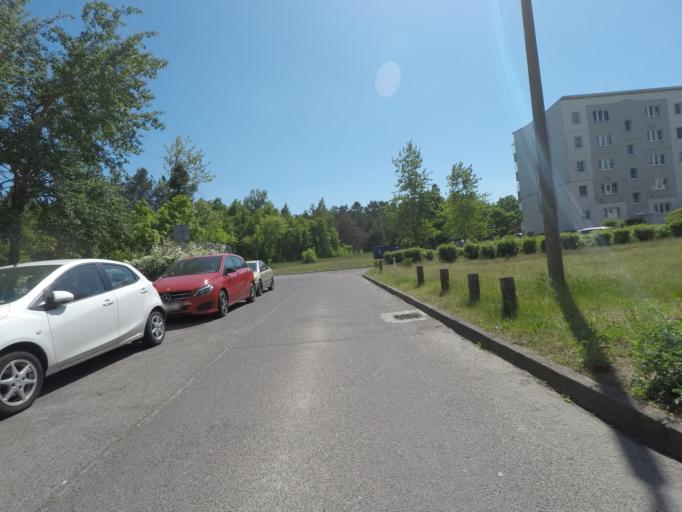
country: DE
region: Brandenburg
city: Eberswalde
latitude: 52.8355
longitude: 13.7497
